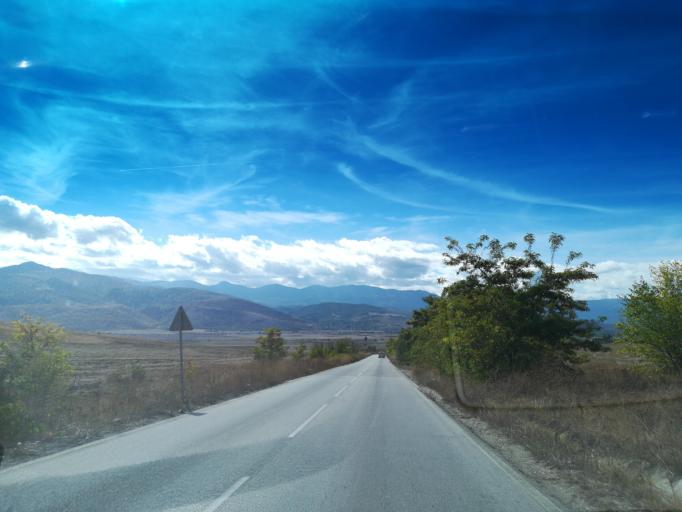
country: BG
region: Plovdiv
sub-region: Obshtina Krichim
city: Krichim
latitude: 42.0958
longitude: 24.4598
